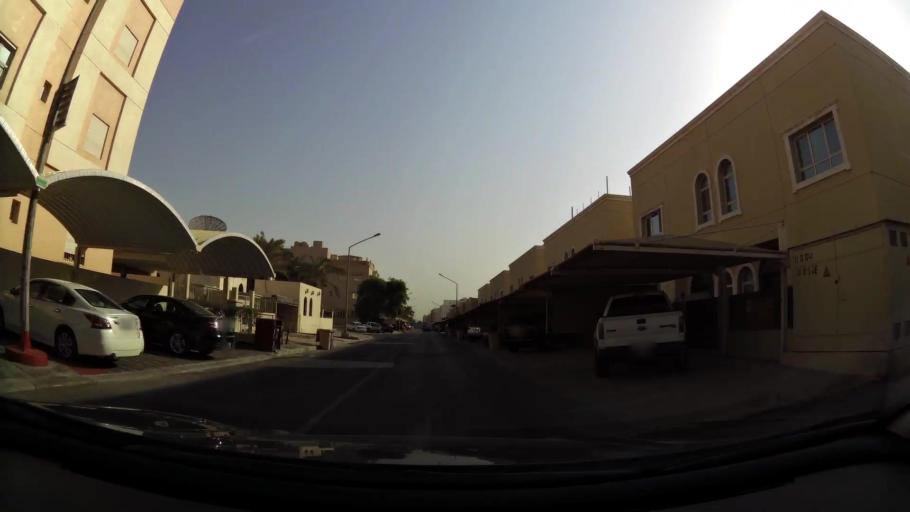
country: KW
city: Bayan
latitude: 29.3129
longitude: 48.0436
